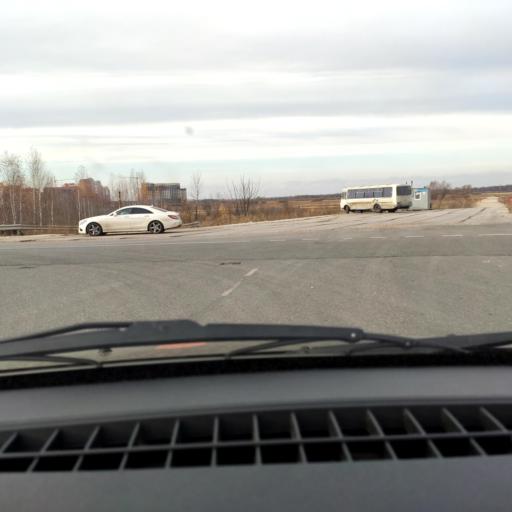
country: RU
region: Bashkortostan
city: Mikhaylovka
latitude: 54.7073
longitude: 55.8542
